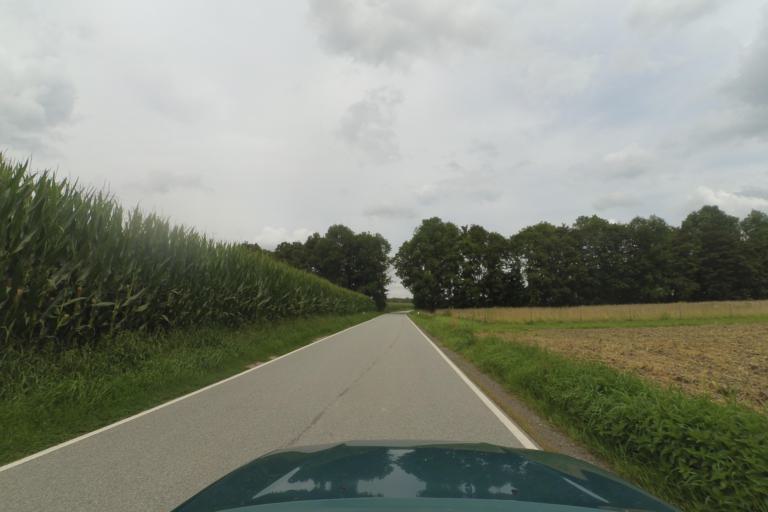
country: DE
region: Bavaria
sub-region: Lower Bavaria
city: Landau an der Isar
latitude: 48.6691
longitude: 12.6716
